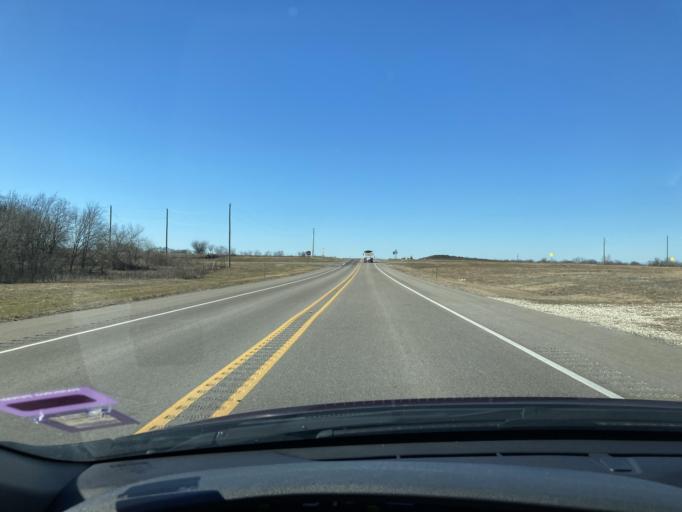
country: US
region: Texas
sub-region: Navarro County
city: Corsicana
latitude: 32.0481
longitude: -96.4801
